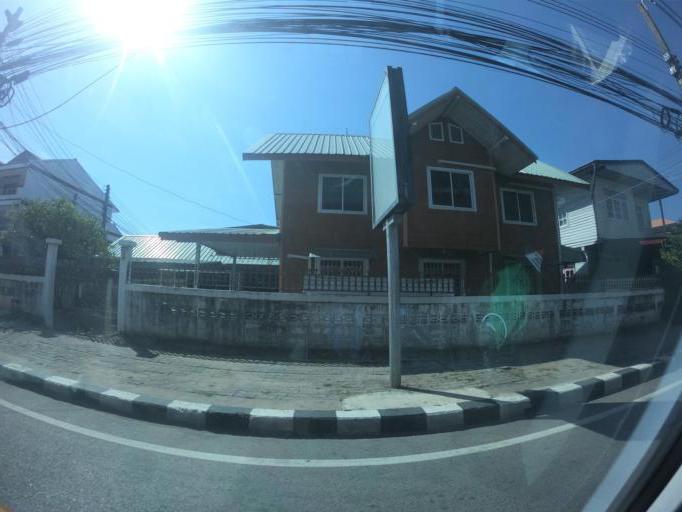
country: TH
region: Khon Kaen
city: Khon Kaen
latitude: 16.4106
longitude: 102.8336
